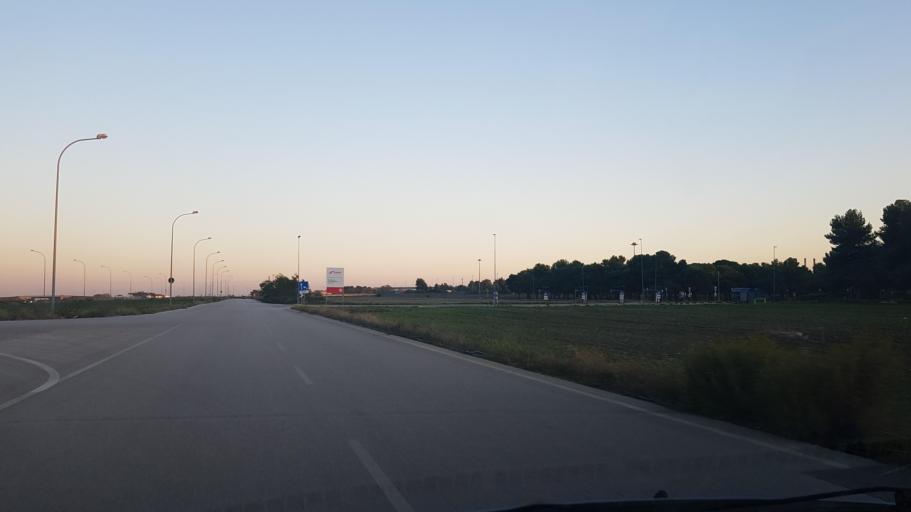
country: IT
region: Apulia
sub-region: Provincia di Foggia
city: Carapelle
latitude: 41.4295
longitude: 15.6454
